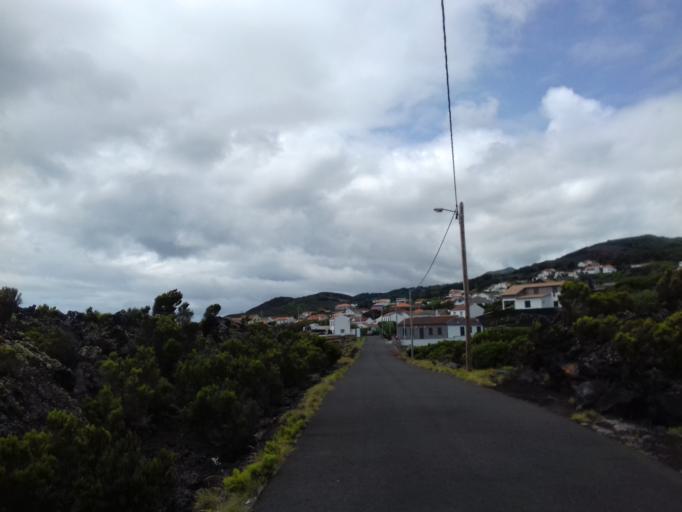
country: PT
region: Azores
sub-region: Sao Roque do Pico
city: Sao Roque do Pico
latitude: 38.4120
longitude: -28.0335
